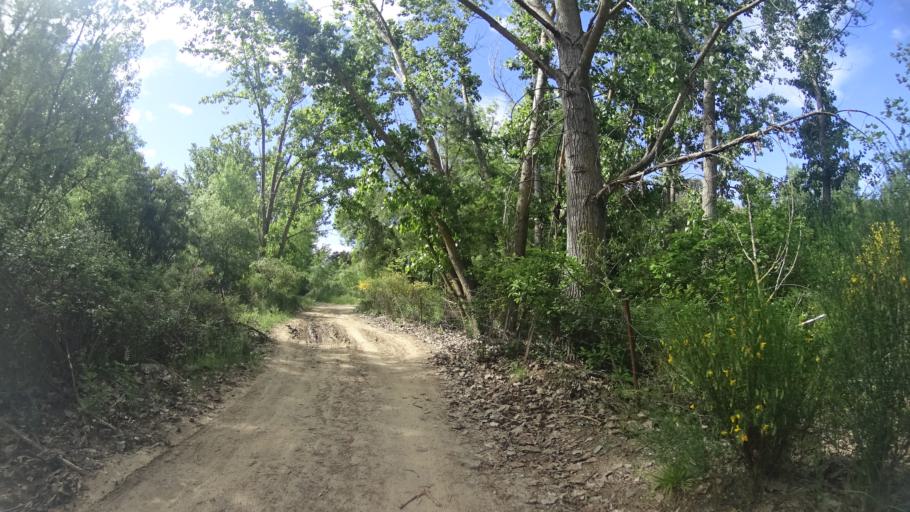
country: ES
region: Madrid
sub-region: Provincia de Madrid
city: Brunete
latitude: 40.4268
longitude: -3.9530
